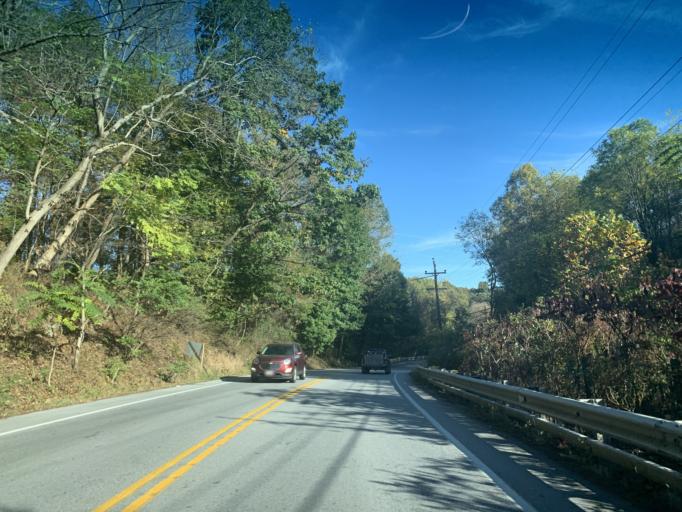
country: US
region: Pennsylvania
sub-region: Chester County
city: Parkesburg
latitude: 39.9454
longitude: -75.9152
